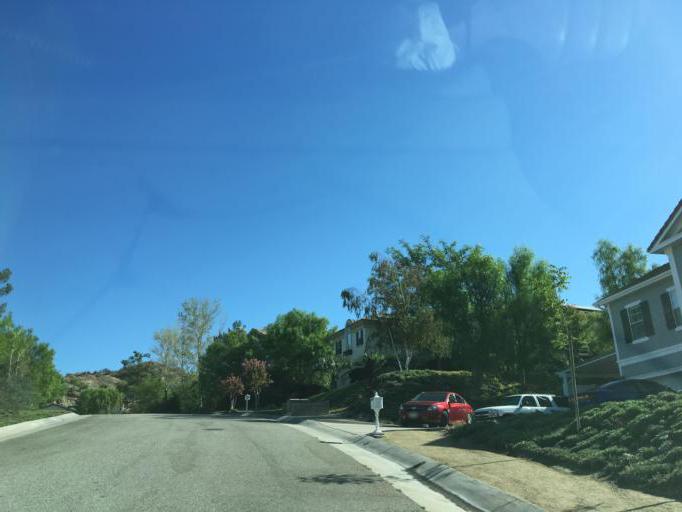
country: US
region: California
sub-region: Los Angeles County
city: Agua Dulce
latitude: 34.4022
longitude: -118.4022
